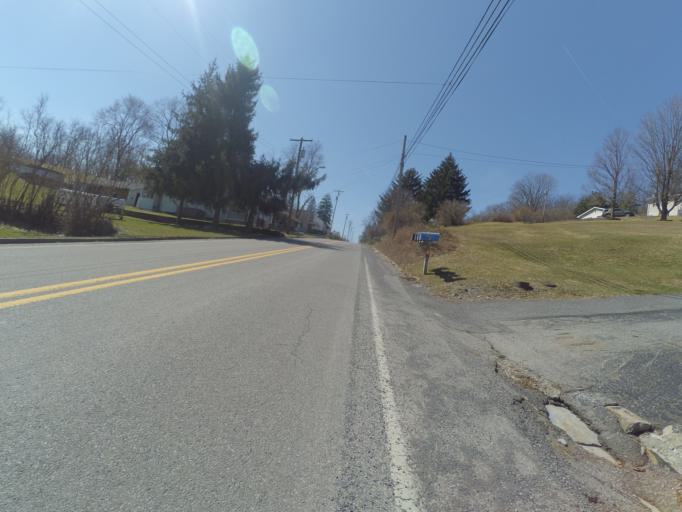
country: US
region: Pennsylvania
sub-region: Centre County
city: Bellefonte
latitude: 40.9112
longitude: -77.7945
